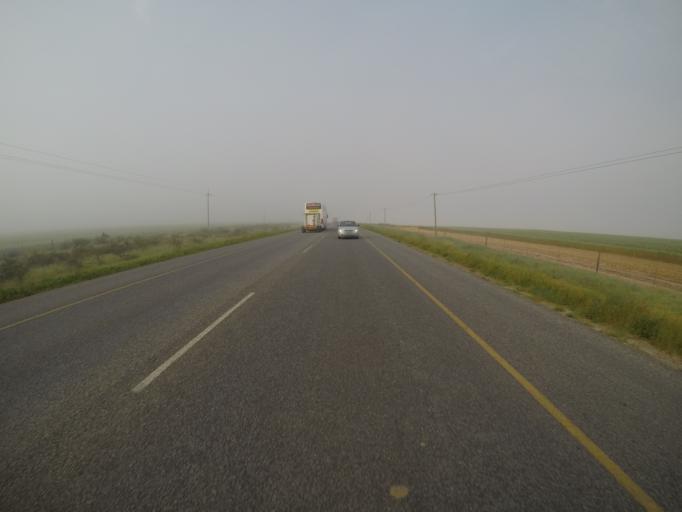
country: ZA
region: Western Cape
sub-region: West Coast District Municipality
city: Malmesbury
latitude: -33.6475
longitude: 18.7121
